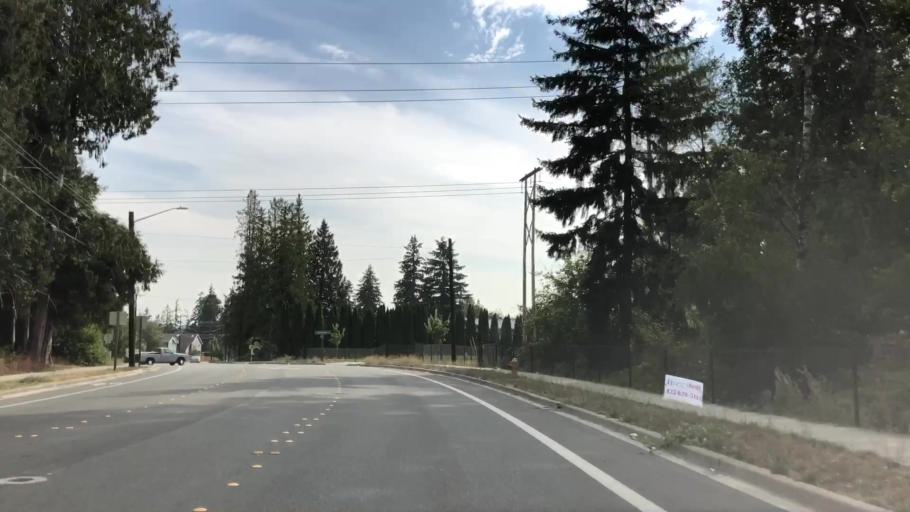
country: US
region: Washington
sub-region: Snohomish County
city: Martha Lake
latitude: 47.8304
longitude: -122.2379
